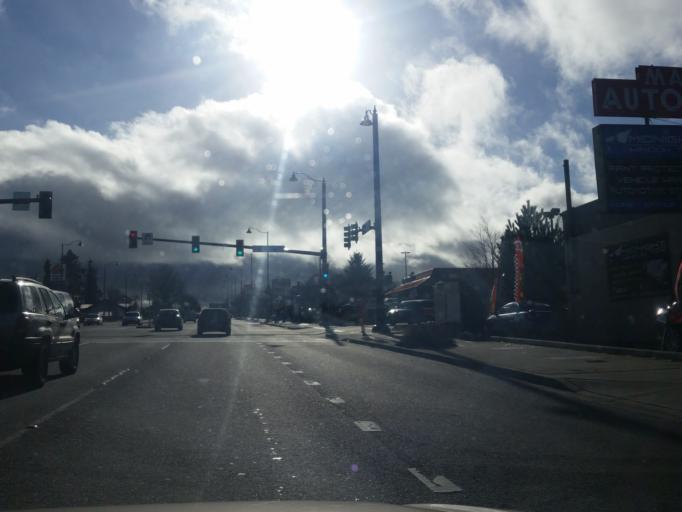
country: US
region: Washington
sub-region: King County
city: Shoreline
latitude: 47.7395
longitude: -122.3454
